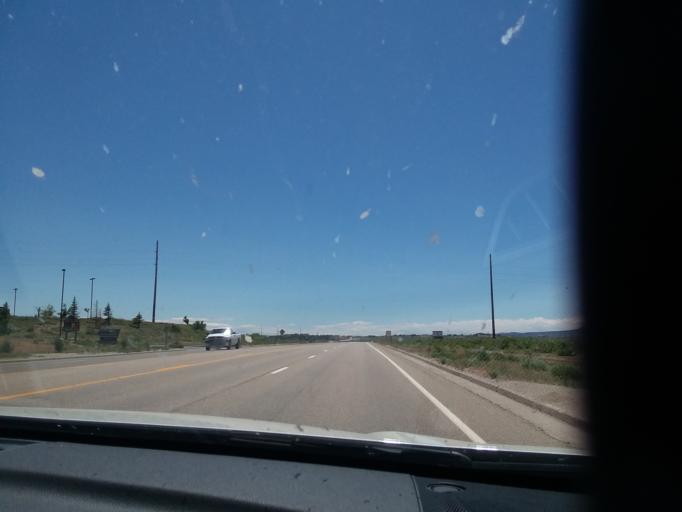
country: US
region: Wyoming
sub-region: Sweetwater County
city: North Rock Springs
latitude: 41.6283
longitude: -109.2323
